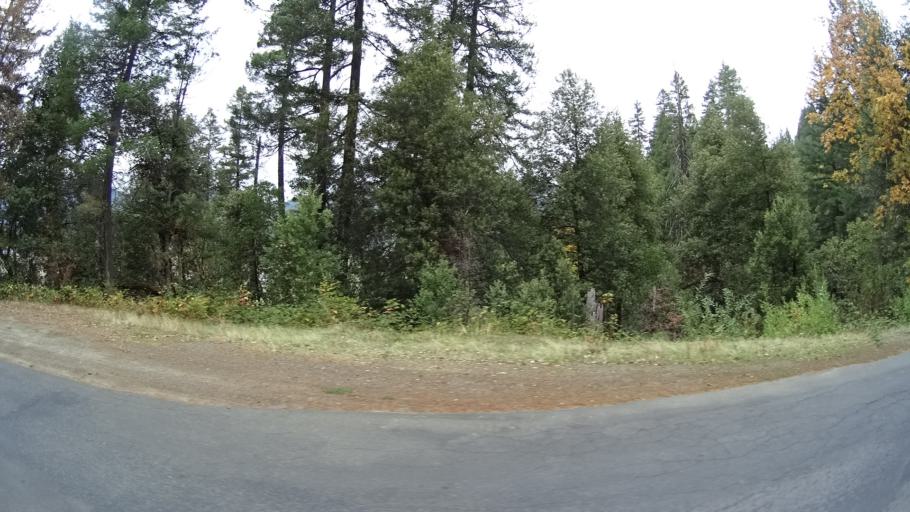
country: US
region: California
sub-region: Siskiyou County
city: Happy Camp
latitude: 41.7959
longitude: -123.3635
